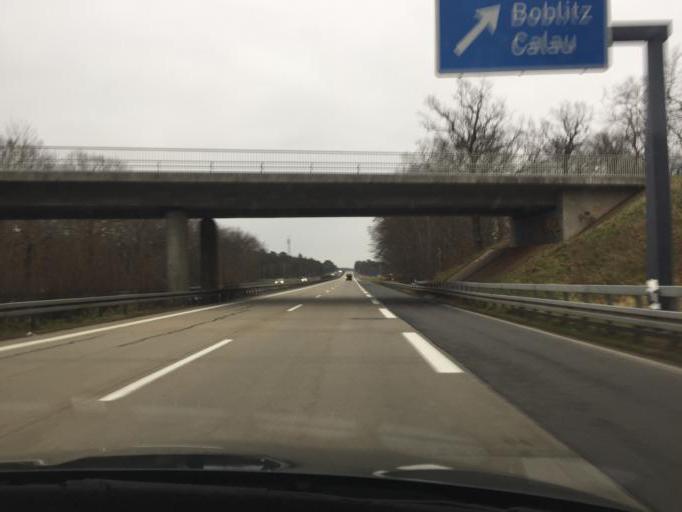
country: DE
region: Brandenburg
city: Lubbenau
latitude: 51.8334
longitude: 13.9750
